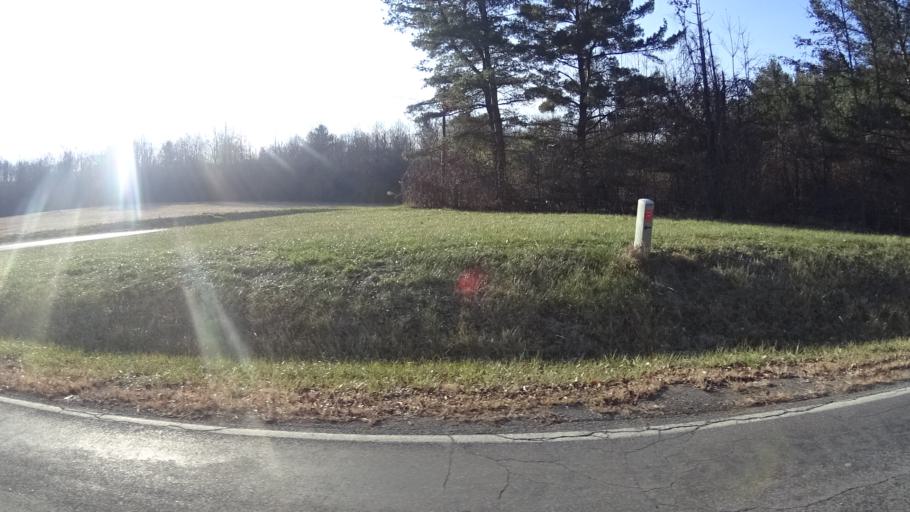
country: US
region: Ohio
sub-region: Lorain County
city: Oberlin
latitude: 41.2653
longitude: -82.2028
